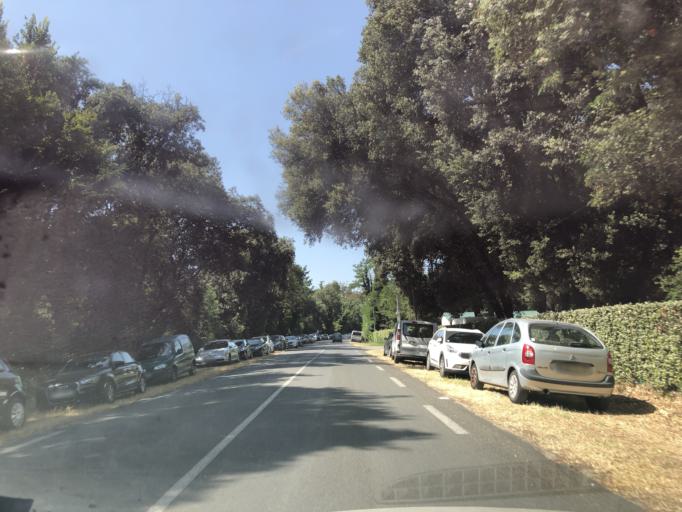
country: FR
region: Poitou-Charentes
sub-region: Departement de la Charente-Maritime
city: Meschers-sur-Gironde
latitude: 45.5664
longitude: -0.9706
